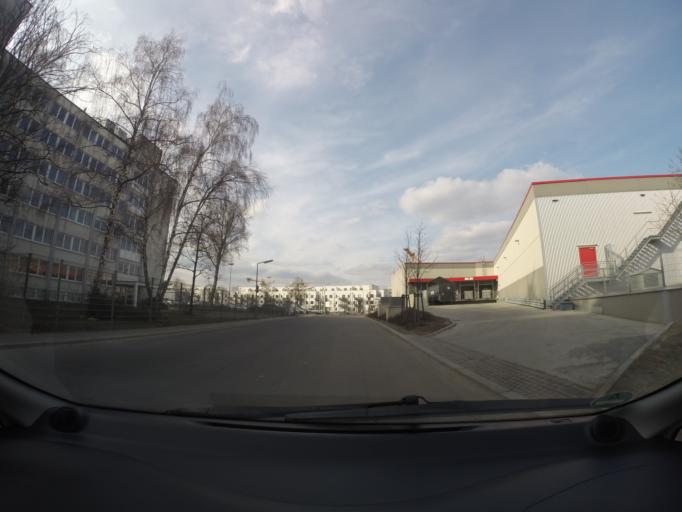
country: DE
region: Berlin
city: Lichterfelde
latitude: 52.4166
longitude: 13.2858
